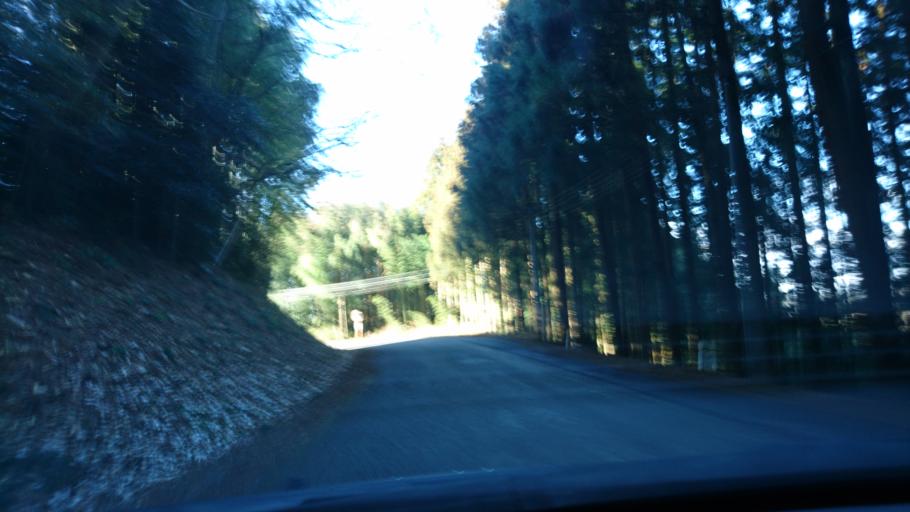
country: JP
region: Iwate
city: Ichinoseki
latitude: 38.8655
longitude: 141.2971
